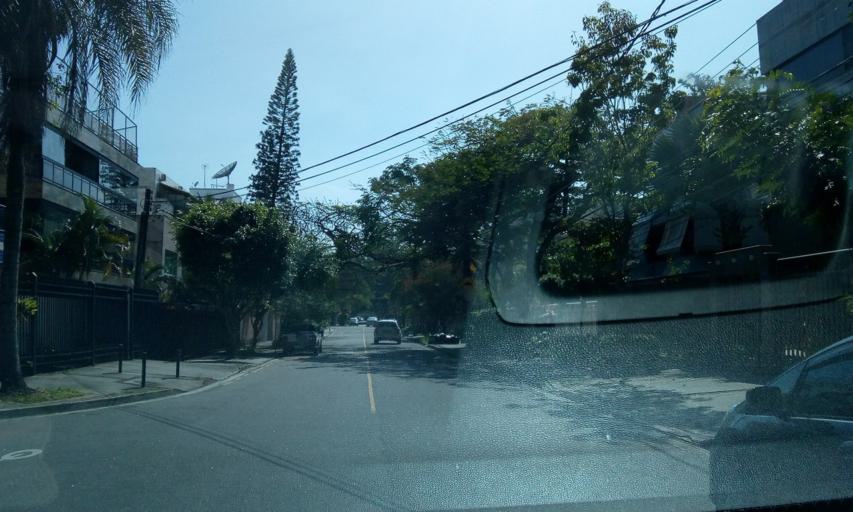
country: BR
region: Rio de Janeiro
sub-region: Nilopolis
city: Nilopolis
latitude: -23.0205
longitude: -43.4576
